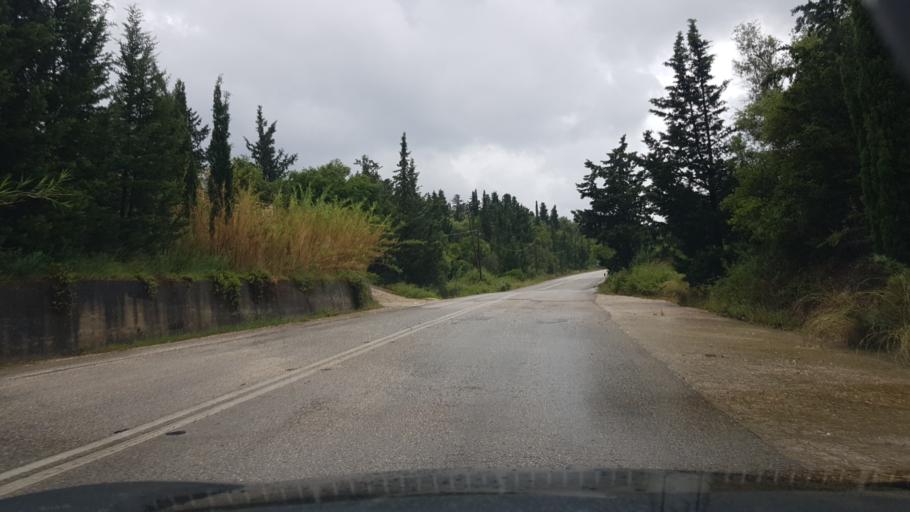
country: GR
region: Ionian Islands
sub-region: Lefkada
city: Nidri
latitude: 38.6349
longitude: 20.6310
